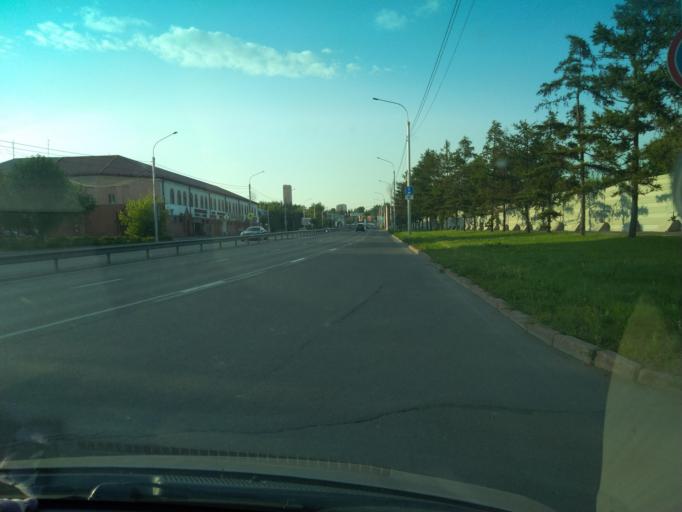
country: RU
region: Krasnoyarskiy
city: Krasnoyarsk
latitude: 56.0207
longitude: 92.8853
